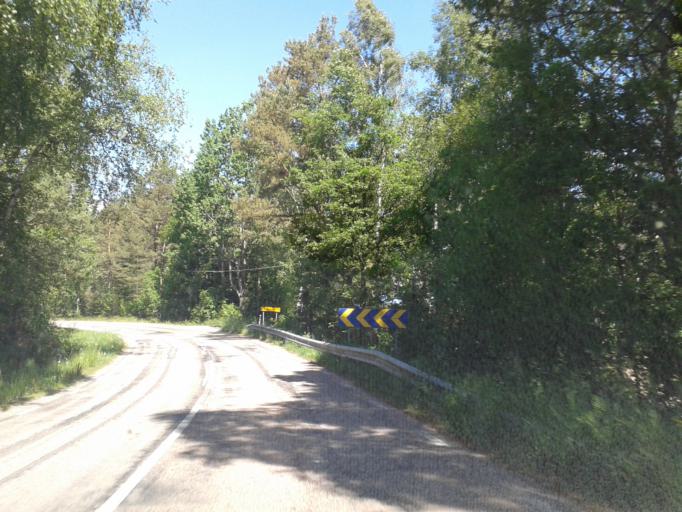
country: SE
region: Vaestra Goetaland
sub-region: Orust
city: Henan
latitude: 58.2832
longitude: 11.7159
